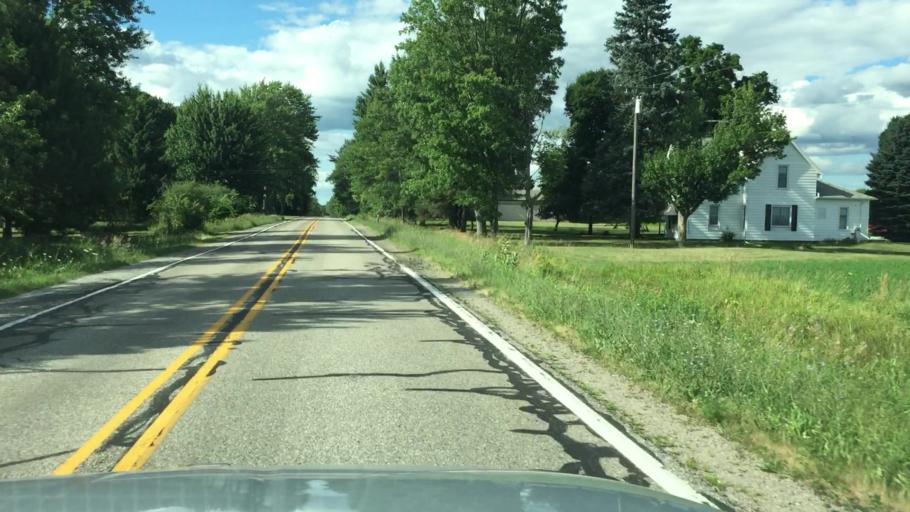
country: US
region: Michigan
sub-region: Saint Clair County
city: Capac
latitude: 43.0932
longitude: -82.9091
